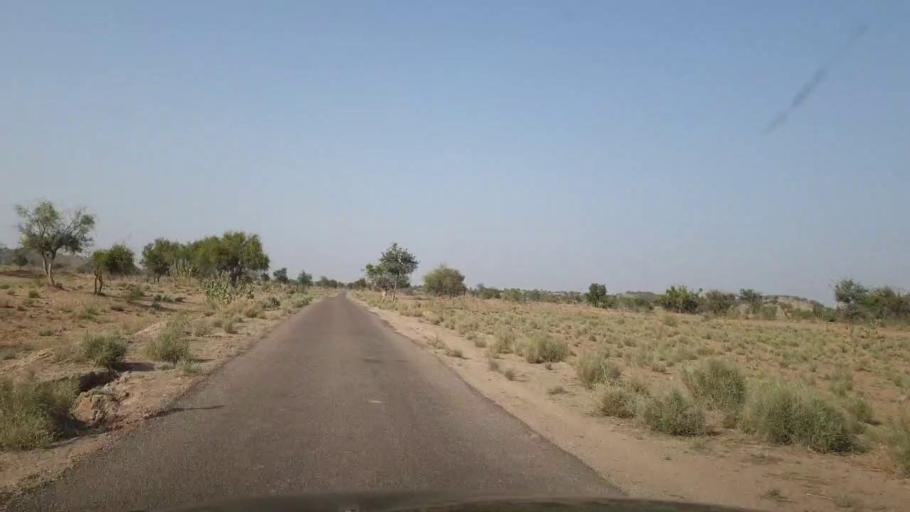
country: PK
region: Sindh
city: Islamkot
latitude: 25.1326
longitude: 70.5172
